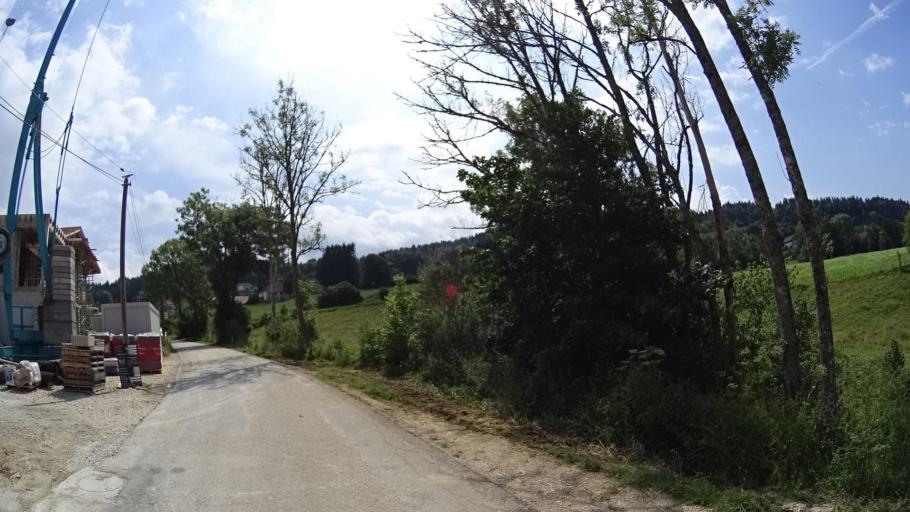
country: FR
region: Franche-Comte
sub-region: Departement du Doubs
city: Les Fourgs
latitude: 46.8363
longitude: 6.3431
